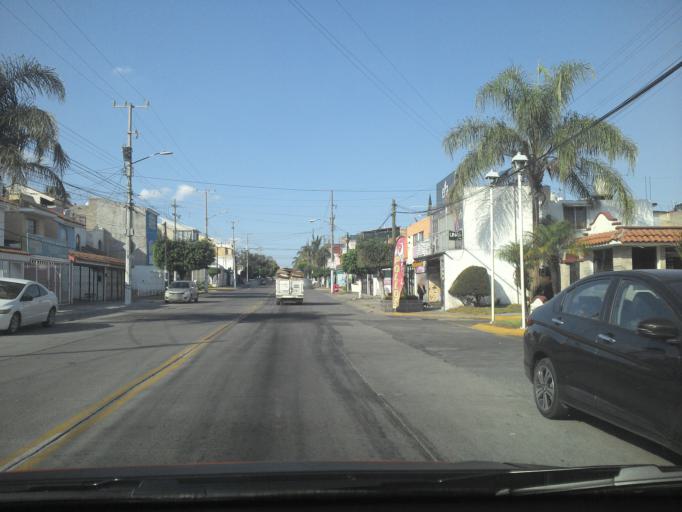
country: MX
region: Jalisco
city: Guadalajara
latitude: 20.6544
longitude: -103.4428
